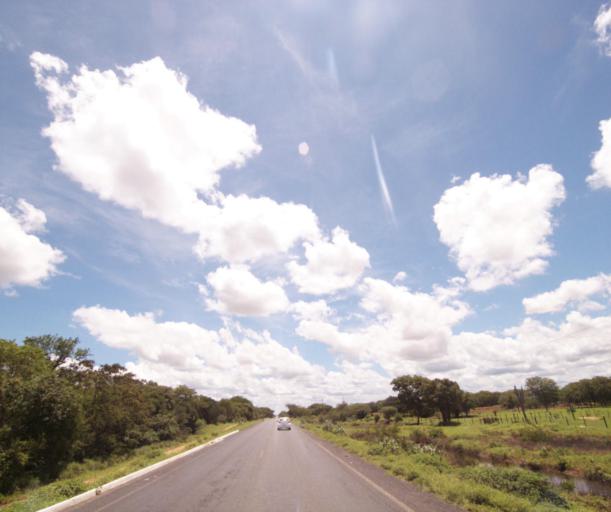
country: BR
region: Bahia
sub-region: Bom Jesus Da Lapa
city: Bom Jesus da Lapa
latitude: -13.2594
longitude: -43.4900
